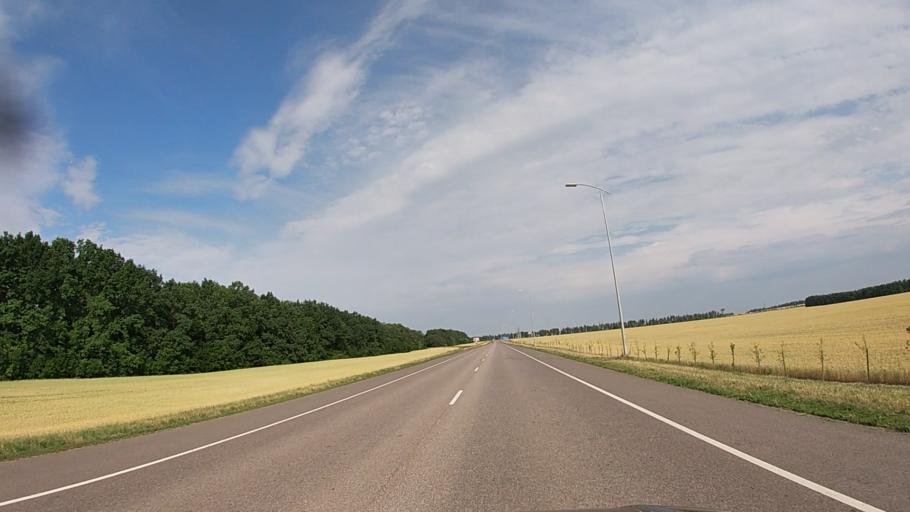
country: RU
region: Belgorod
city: Proletarskiy
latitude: 50.8269
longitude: 35.7779
